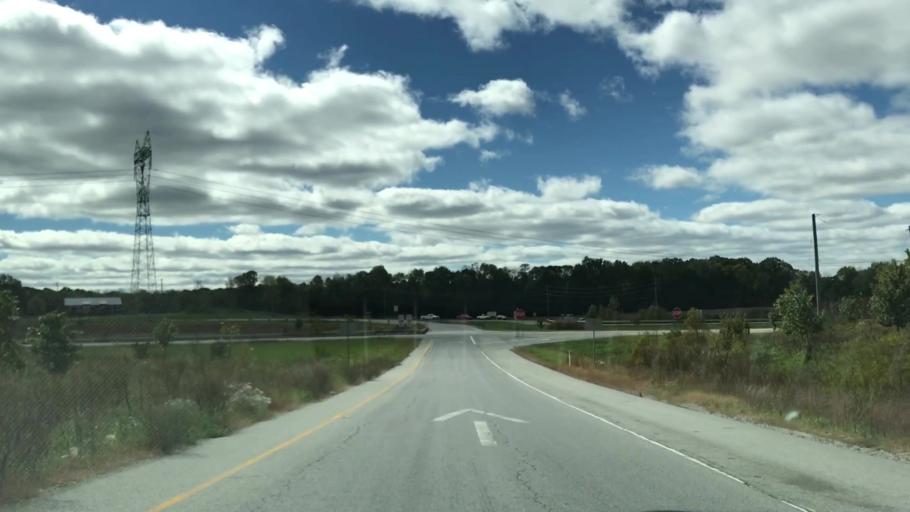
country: US
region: Indiana
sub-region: Hamilton County
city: Westfield
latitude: 40.0959
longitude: -86.1287
